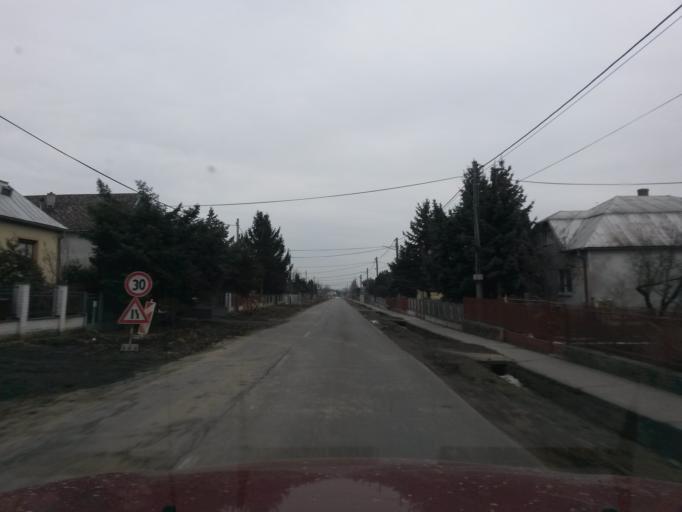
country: SK
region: Kosicky
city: Trebisov
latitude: 48.6952
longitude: 21.8087
